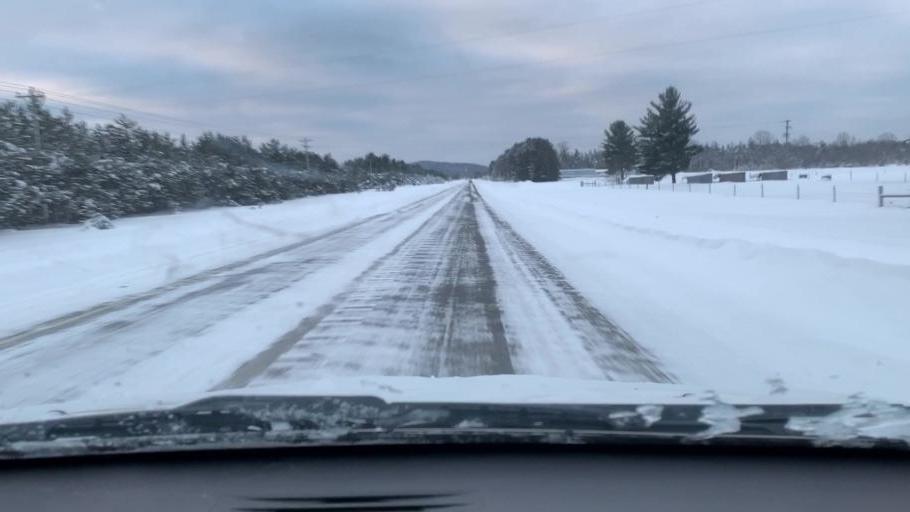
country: US
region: Michigan
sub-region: Antrim County
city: Mancelona
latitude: 44.9281
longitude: -85.0509
